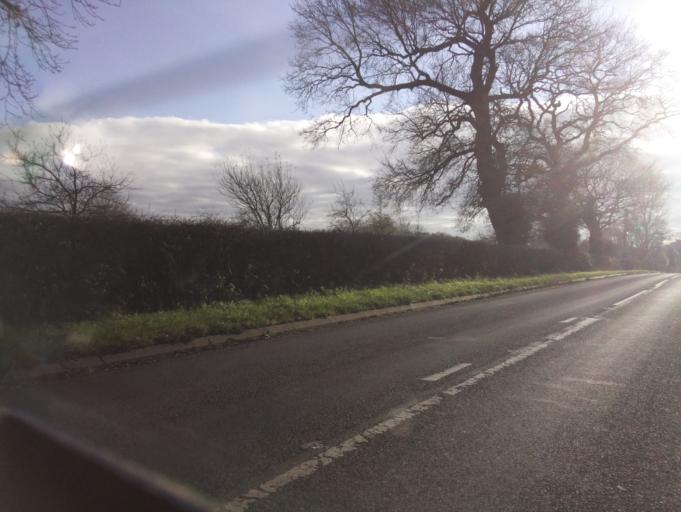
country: GB
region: England
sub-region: Staffordshire
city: Barton under Needwood
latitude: 52.8078
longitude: -1.7370
